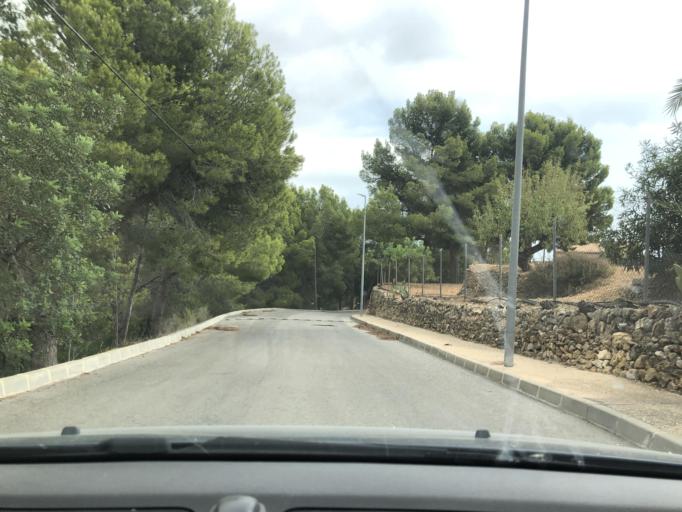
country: ES
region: Valencia
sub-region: Provincia de Alicante
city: Altea
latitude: 38.6397
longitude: -0.0686
